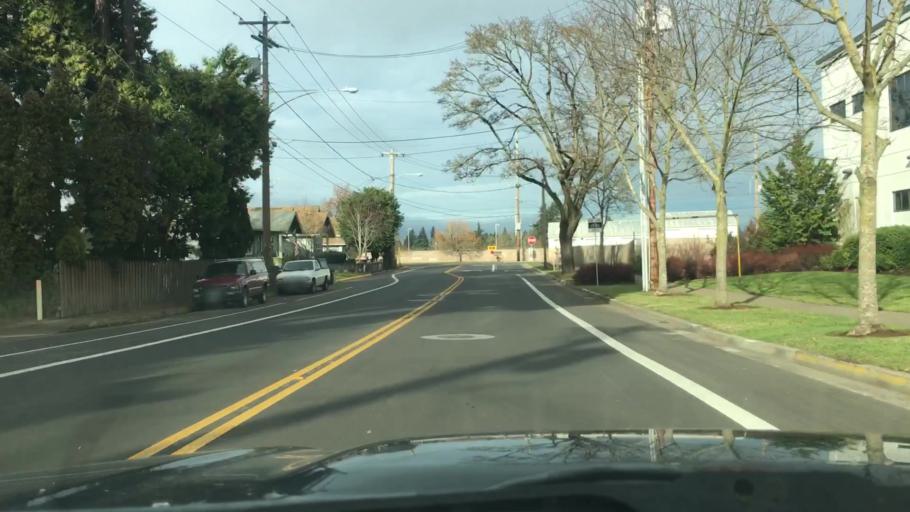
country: US
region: Oregon
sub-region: Lane County
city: Eugene
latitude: 44.0622
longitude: -123.1226
